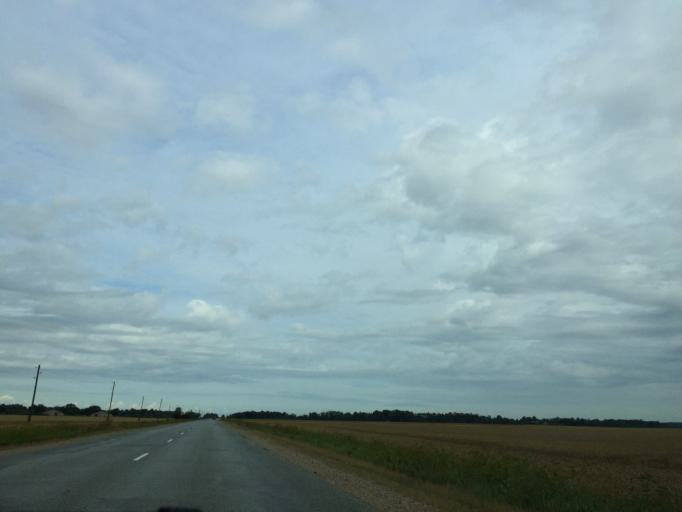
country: LV
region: Engure
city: Smarde
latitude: 56.8020
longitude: 23.3636
